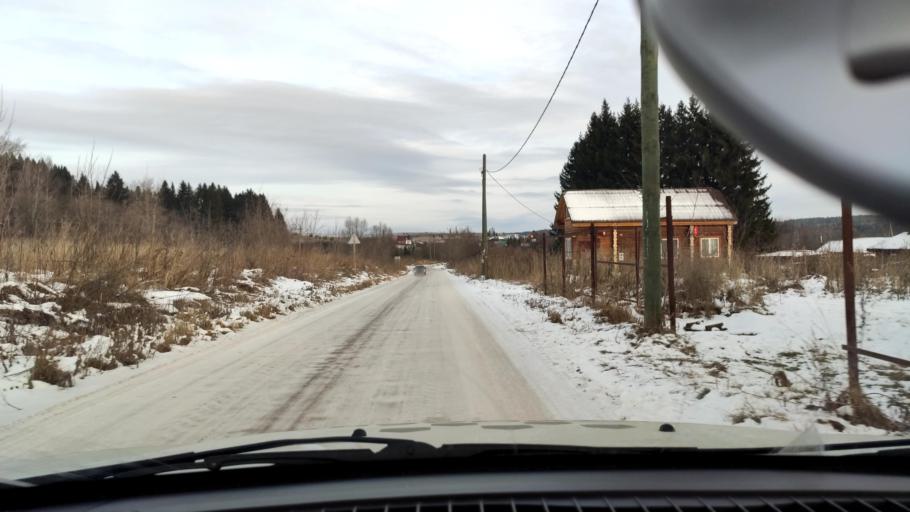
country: RU
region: Perm
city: Lobanovo
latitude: 57.8269
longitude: 56.3541
